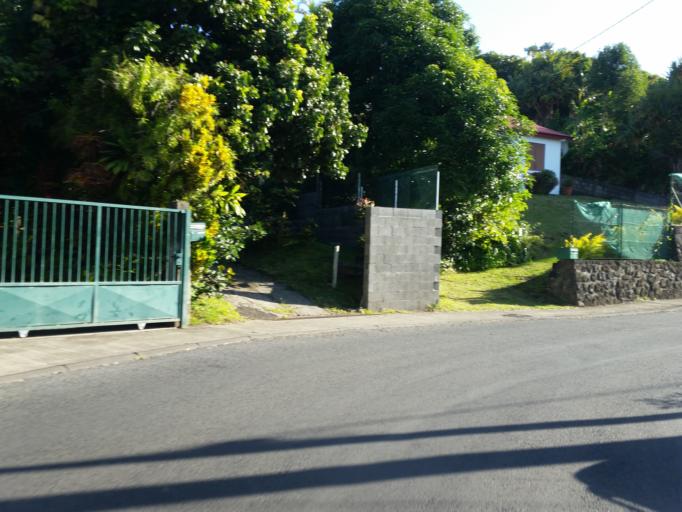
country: RE
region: Reunion
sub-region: Reunion
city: Sainte-Marie
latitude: -20.9265
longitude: 55.5238
